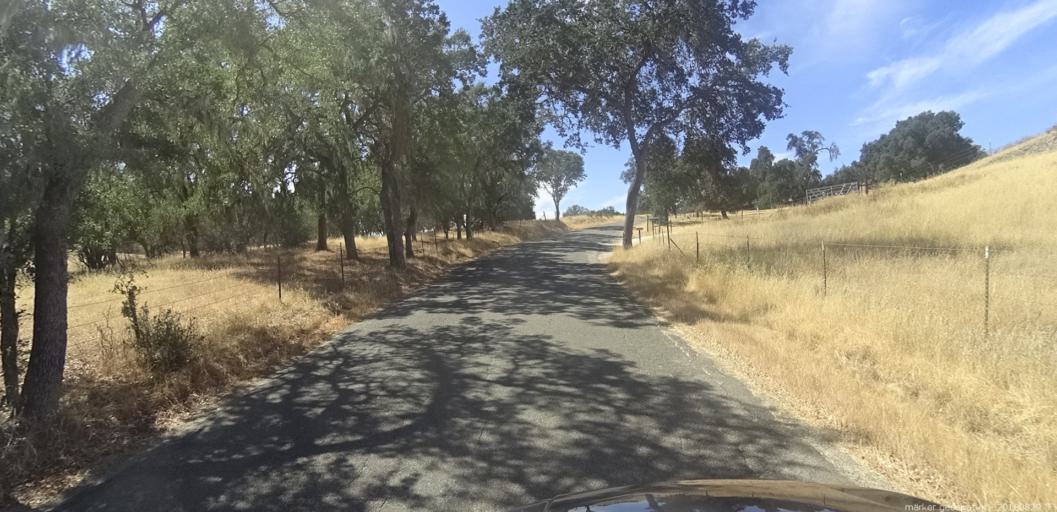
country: US
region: California
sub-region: San Luis Obispo County
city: Lake Nacimiento
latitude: 35.8188
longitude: -121.0532
